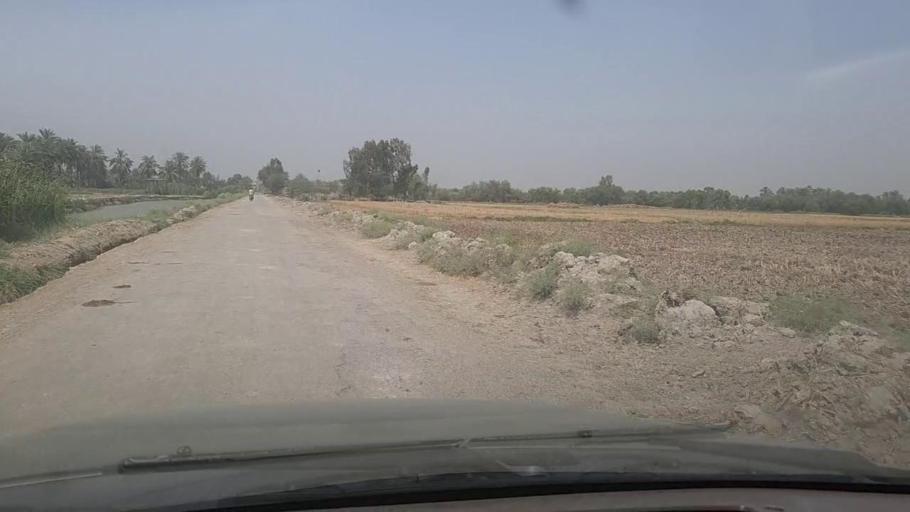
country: PK
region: Sindh
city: Madeji
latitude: 27.7978
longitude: 68.4279
